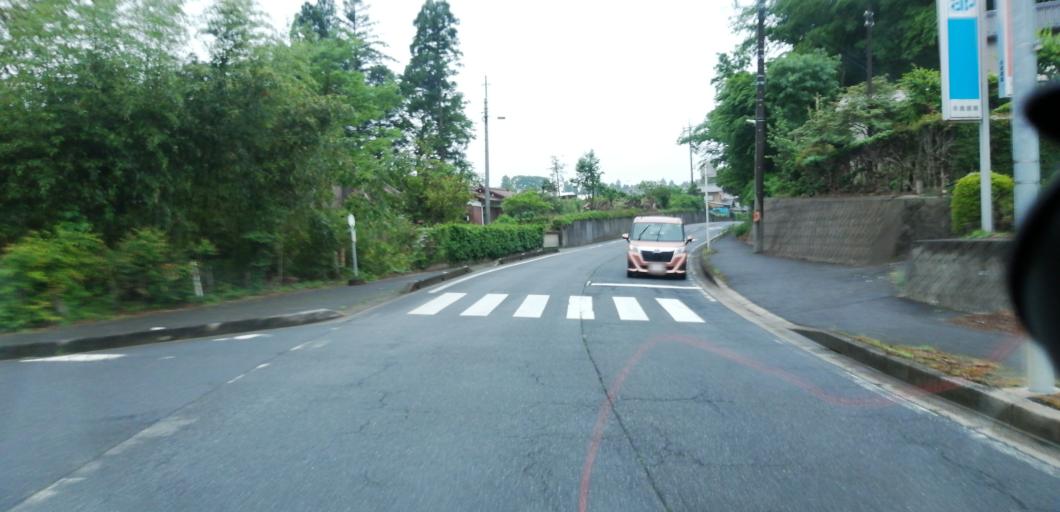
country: JP
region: Chiba
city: Oami
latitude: 35.5533
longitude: 140.2374
